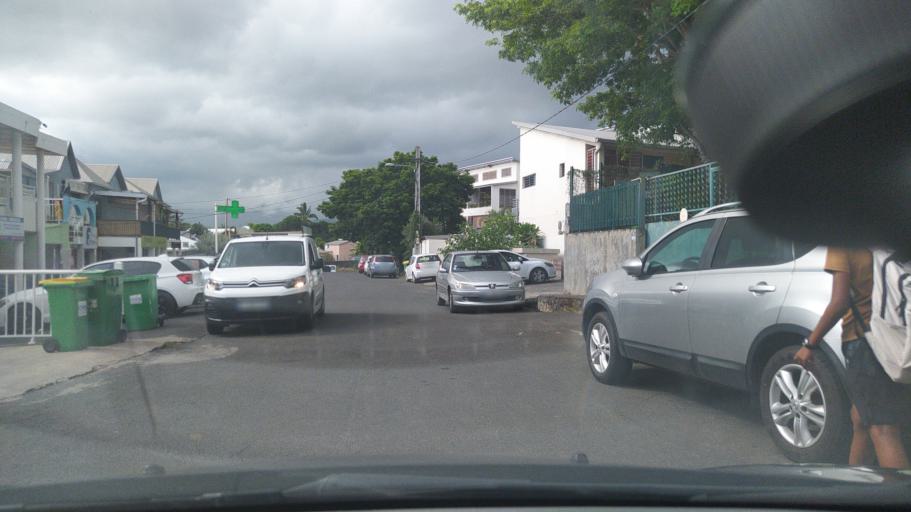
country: RE
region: Reunion
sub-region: Reunion
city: Saint-Pierre
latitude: -21.3115
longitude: 55.4727
